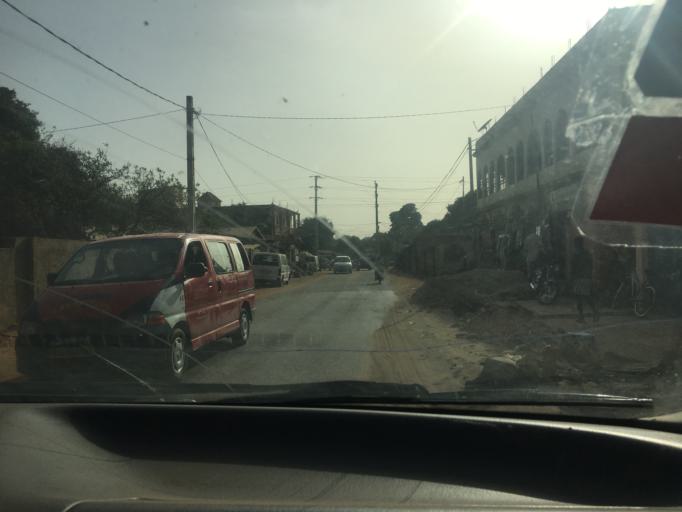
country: GM
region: Western
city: Abuko
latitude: 13.4034
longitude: -16.6727
